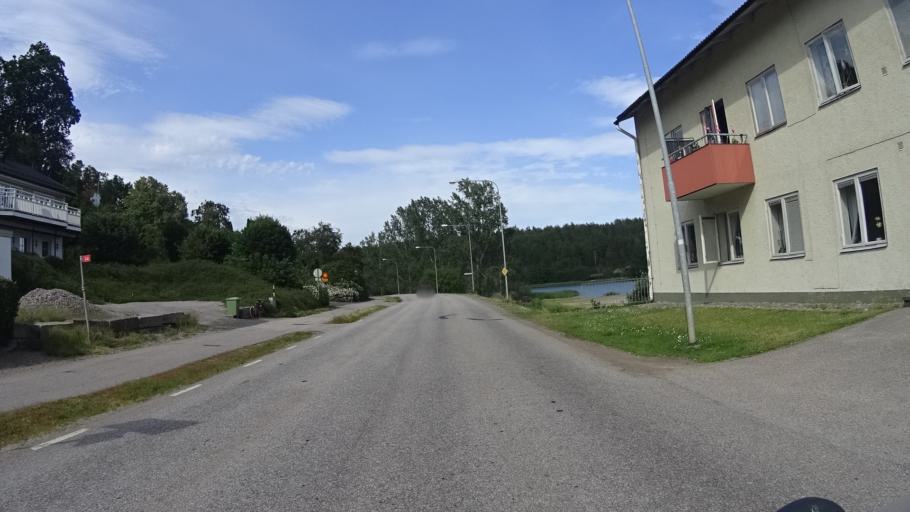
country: SE
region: Kalmar
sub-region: Vasterviks Kommun
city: Gamleby
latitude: 57.9007
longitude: 16.4109
